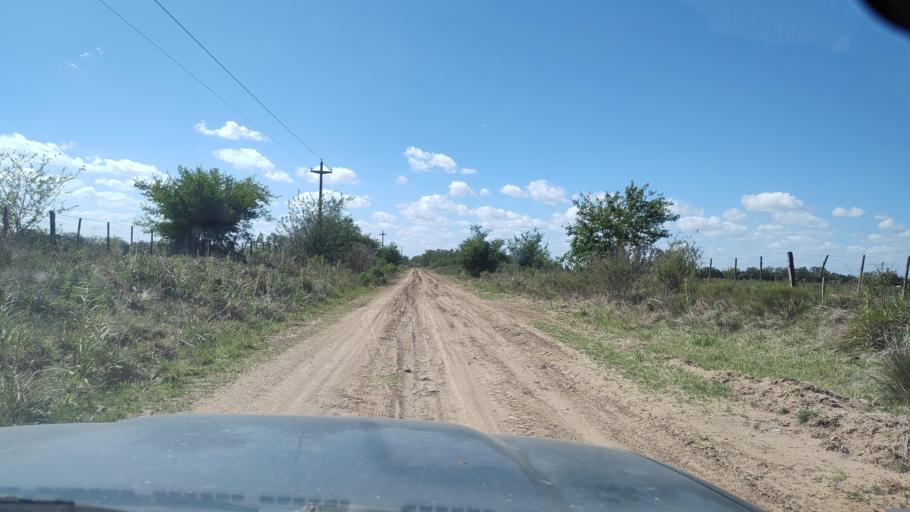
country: AR
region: Buenos Aires
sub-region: Partido de Lujan
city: Lujan
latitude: -34.5246
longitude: -59.1558
